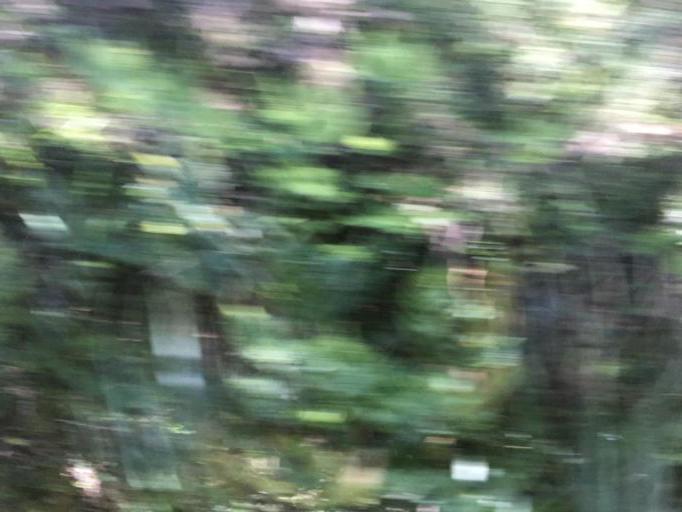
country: TW
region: Taiwan
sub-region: Yilan
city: Yilan
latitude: 24.5340
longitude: 121.5203
